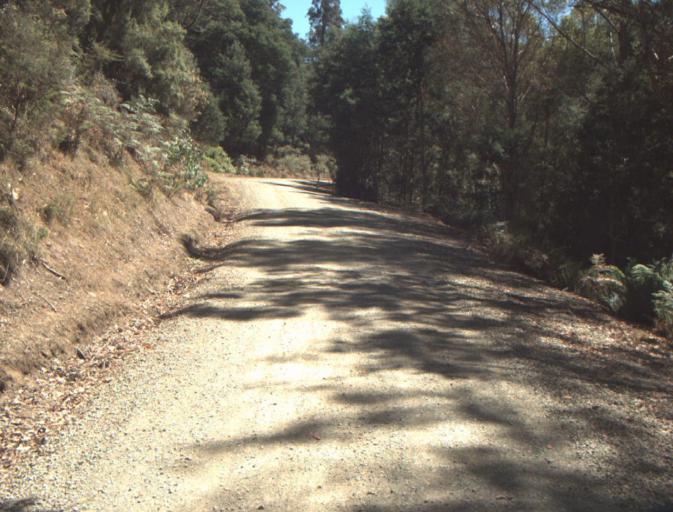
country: AU
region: Tasmania
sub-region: Dorset
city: Scottsdale
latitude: -41.3018
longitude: 147.3643
